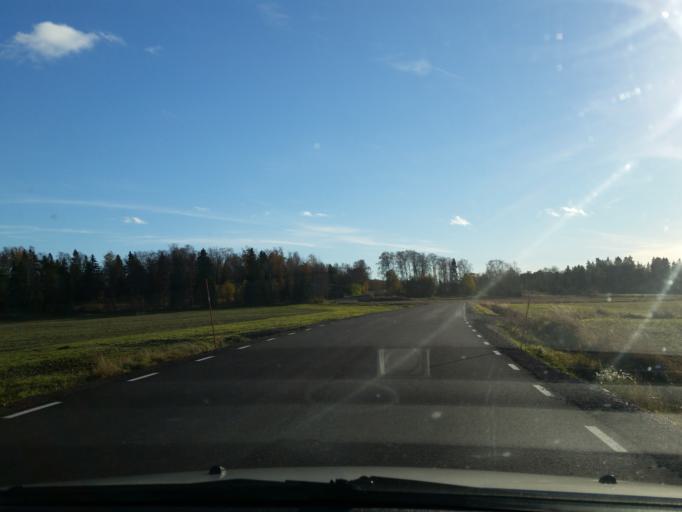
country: AX
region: Alands landsbygd
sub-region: Jomala
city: Jomala
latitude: 60.1931
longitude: 19.9598
